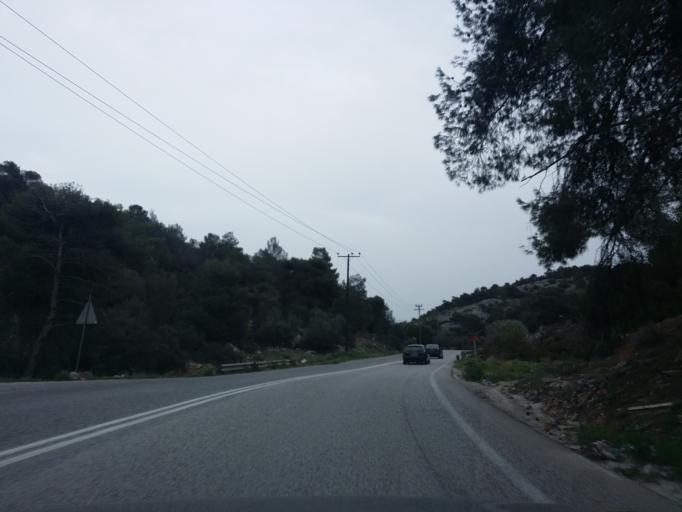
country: GR
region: Attica
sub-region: Nomarchia Dytikis Attikis
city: Mandra
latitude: 38.0973
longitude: 23.4647
